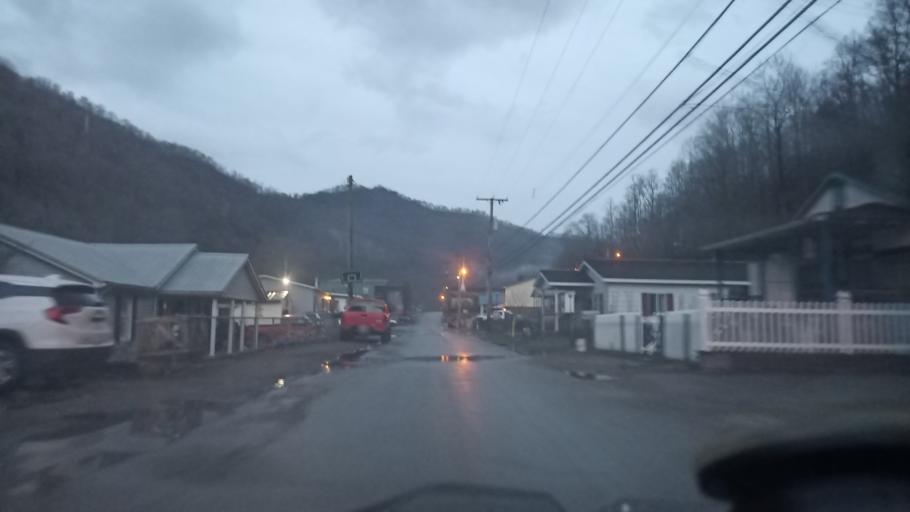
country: US
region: West Virginia
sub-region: Logan County
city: Mallory
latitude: 37.7223
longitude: -81.8736
